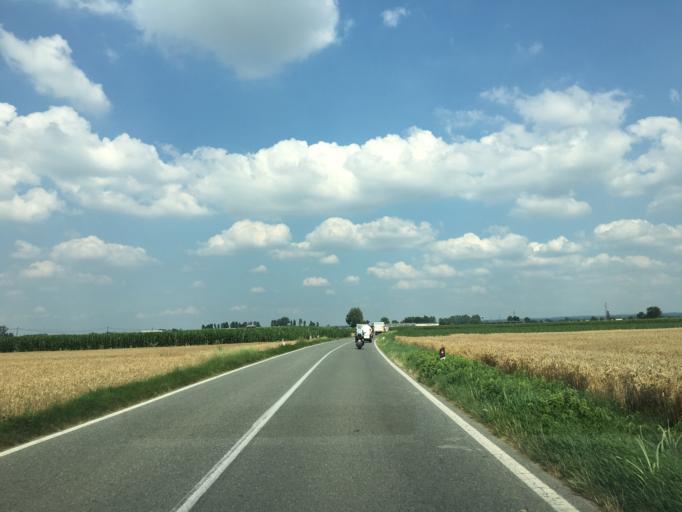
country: IT
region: Piedmont
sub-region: Provincia di Cuneo
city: Racconigi
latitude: 44.7745
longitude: 7.7088
